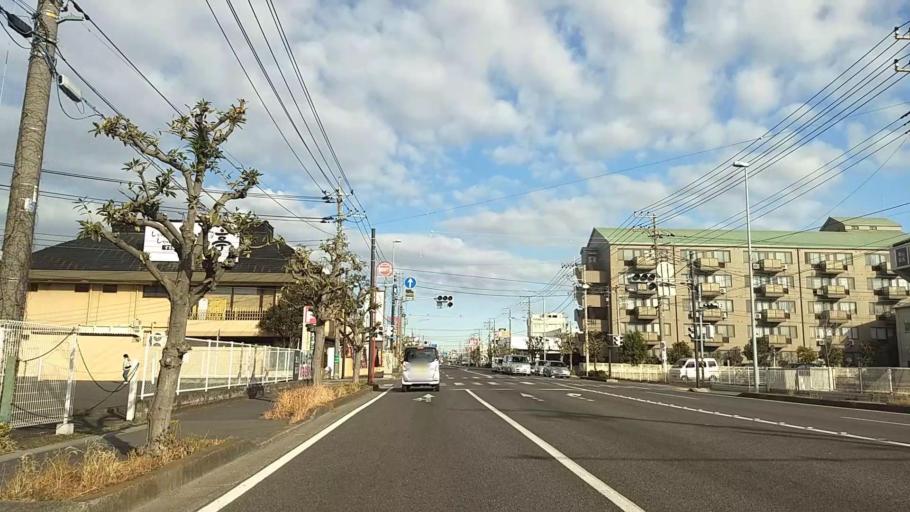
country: JP
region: Kanagawa
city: Hiratsuka
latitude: 35.3429
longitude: 139.3562
